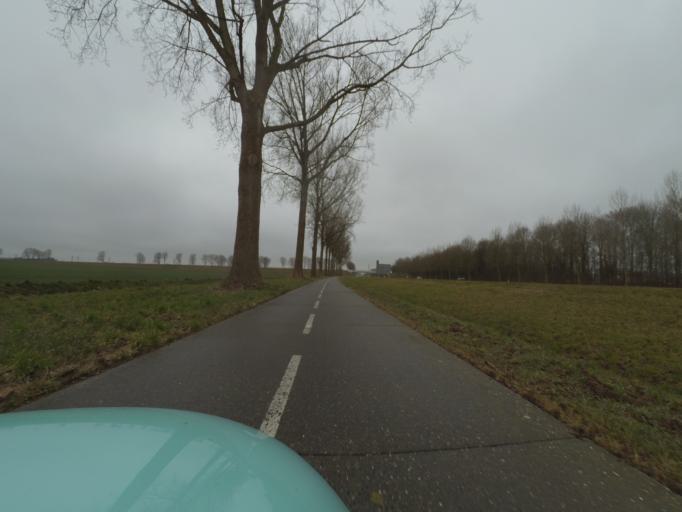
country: NL
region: Flevoland
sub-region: Gemeente Dronten
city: Dronten
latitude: 52.5356
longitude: 5.7394
